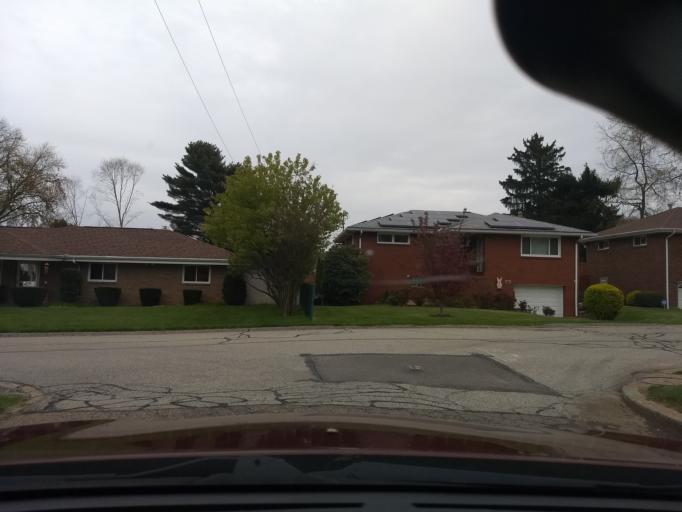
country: US
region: Pennsylvania
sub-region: Allegheny County
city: McKees Rocks
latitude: 40.4579
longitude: -80.0810
